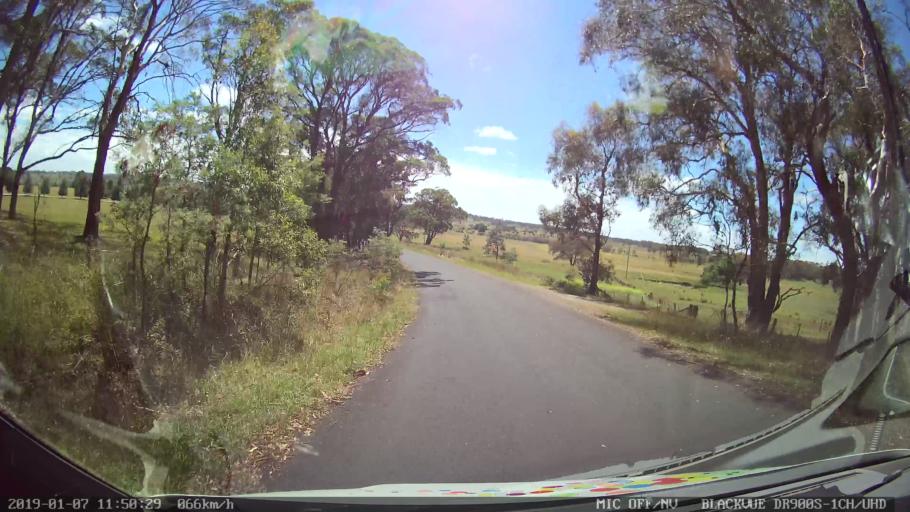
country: AU
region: New South Wales
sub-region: Guyra
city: Guyra
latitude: -30.3126
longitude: 151.6365
